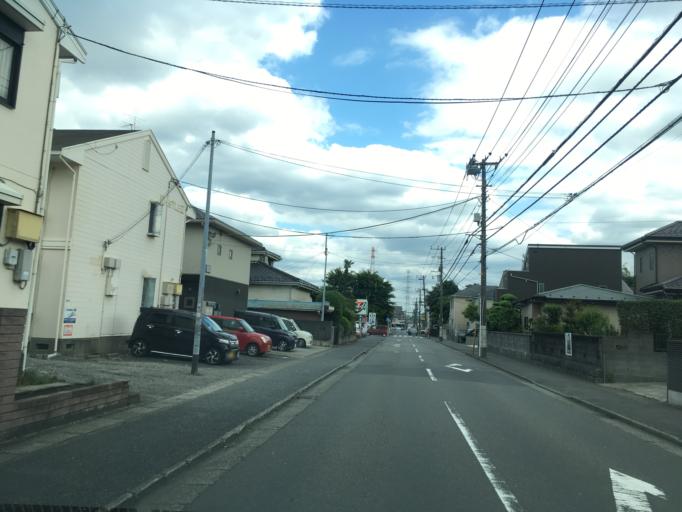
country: JP
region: Tokyo
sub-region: Machida-shi
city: Machida
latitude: 35.5636
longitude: 139.4025
